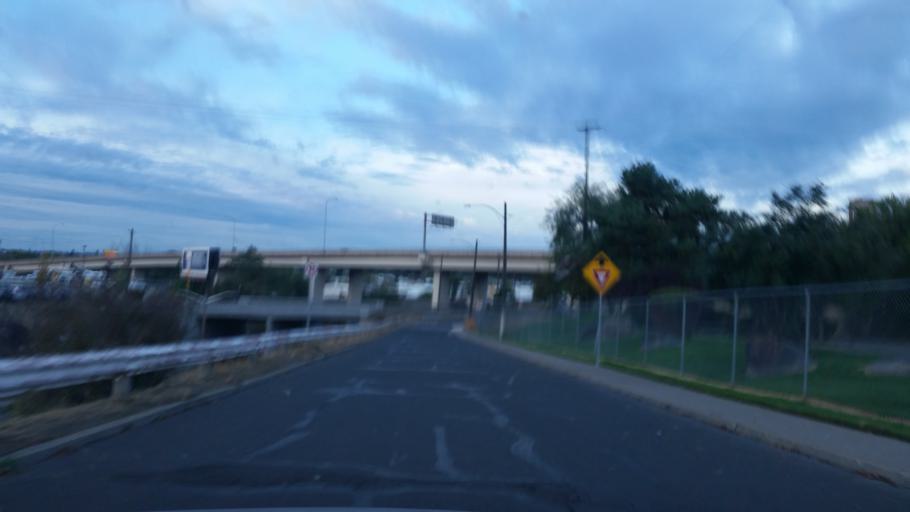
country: US
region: Washington
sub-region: Spokane County
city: Spokane
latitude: 47.6562
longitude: -117.3962
